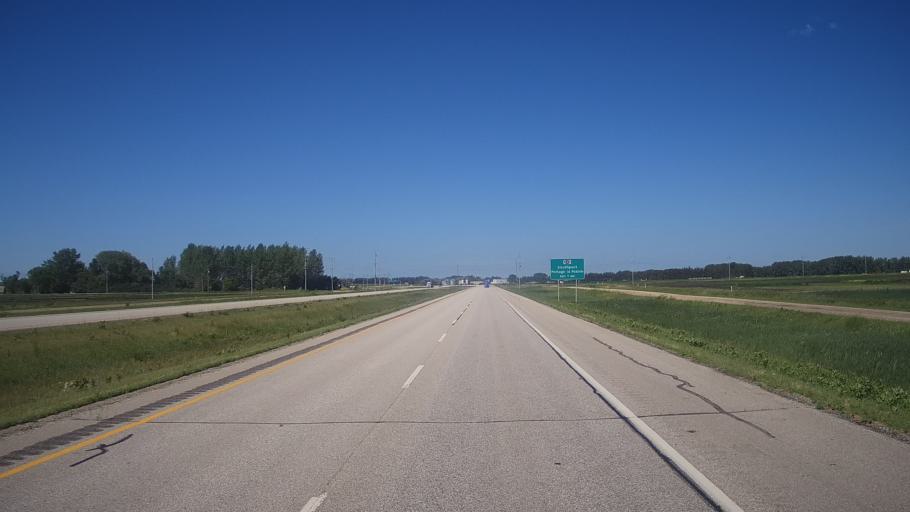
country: CA
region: Manitoba
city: Portage la Prairie
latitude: 49.9597
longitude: -98.2526
